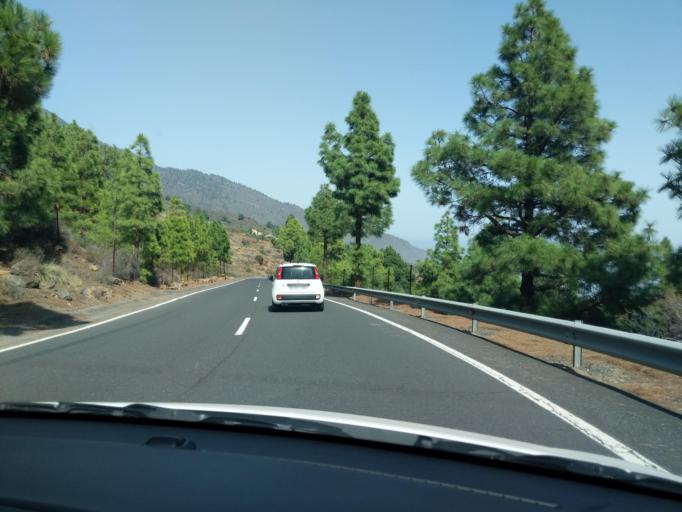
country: ES
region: Canary Islands
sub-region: Provincia de Santa Cruz de Tenerife
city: Arafo
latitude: 28.3525
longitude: -16.4264
